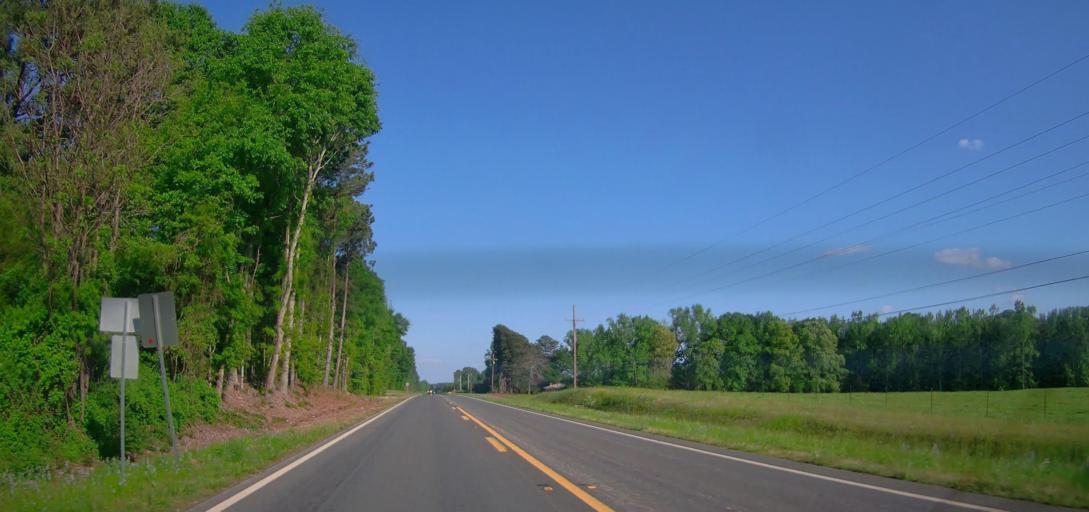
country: US
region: Georgia
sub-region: Walton County
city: Social Circle
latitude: 33.6168
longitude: -83.5982
